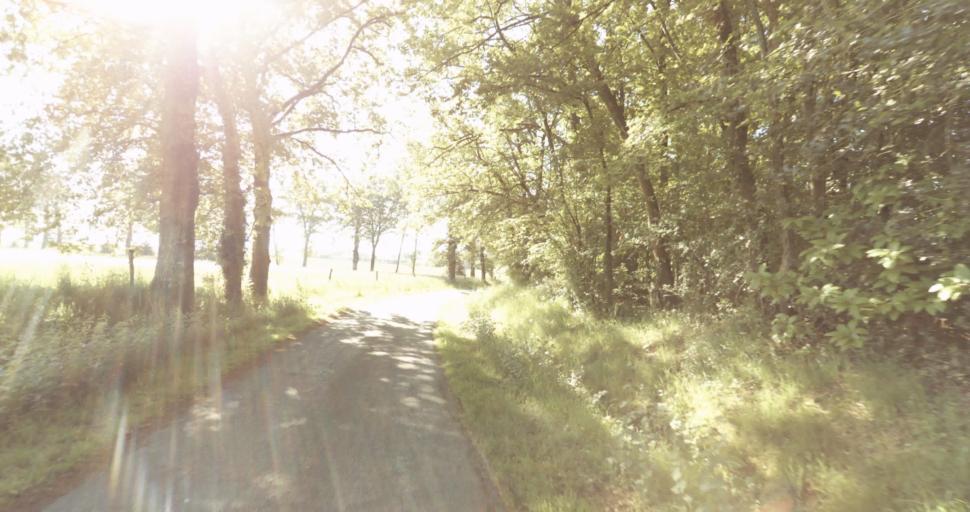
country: FR
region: Limousin
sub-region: Departement de la Haute-Vienne
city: Bosmie-l'Aiguille
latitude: 45.7285
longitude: 1.2351
